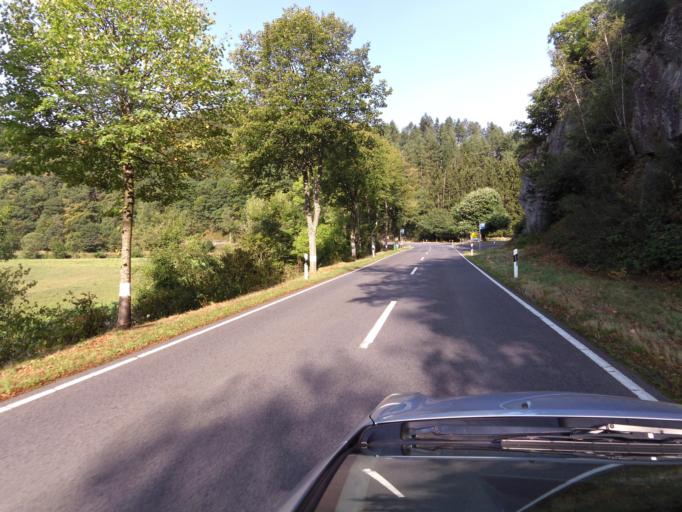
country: LU
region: Diekirch
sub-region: Canton de Diekirch
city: Bourscheid
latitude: 49.9318
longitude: 6.0711
